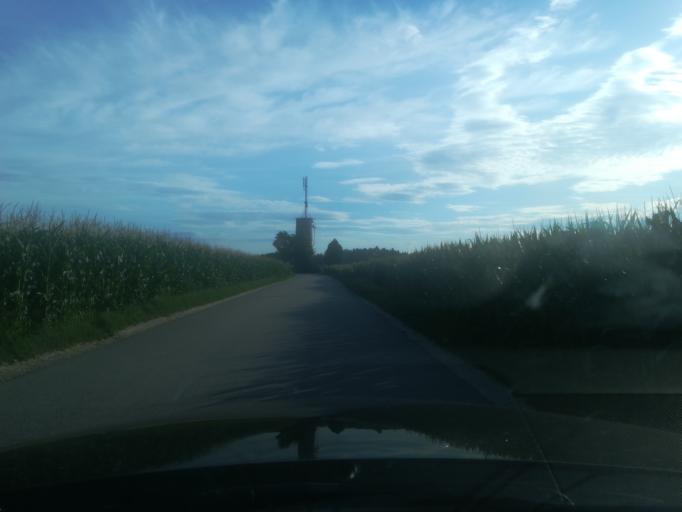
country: AT
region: Upper Austria
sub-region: Wels-Land
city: Marchtrenk
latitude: 48.1566
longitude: 14.1689
